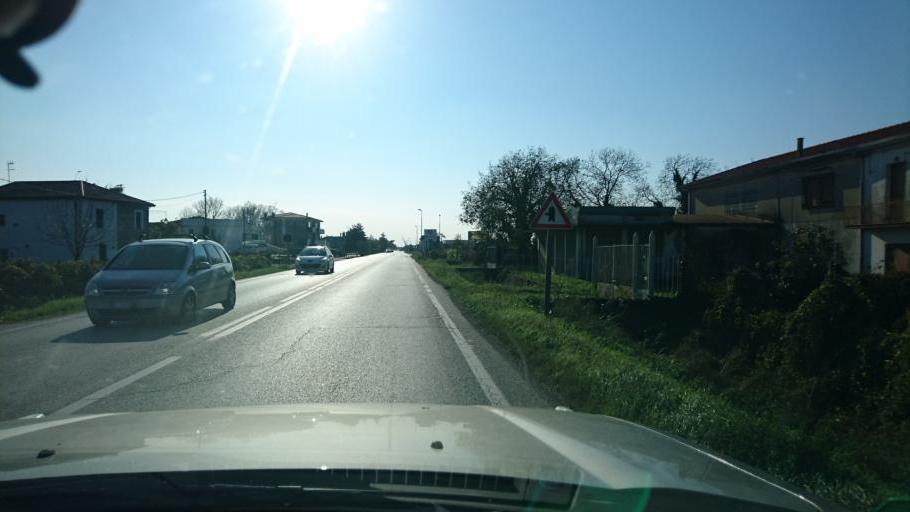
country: IT
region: Veneto
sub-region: Provincia di Padova
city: Monselice
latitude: 45.2223
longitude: 11.7551
